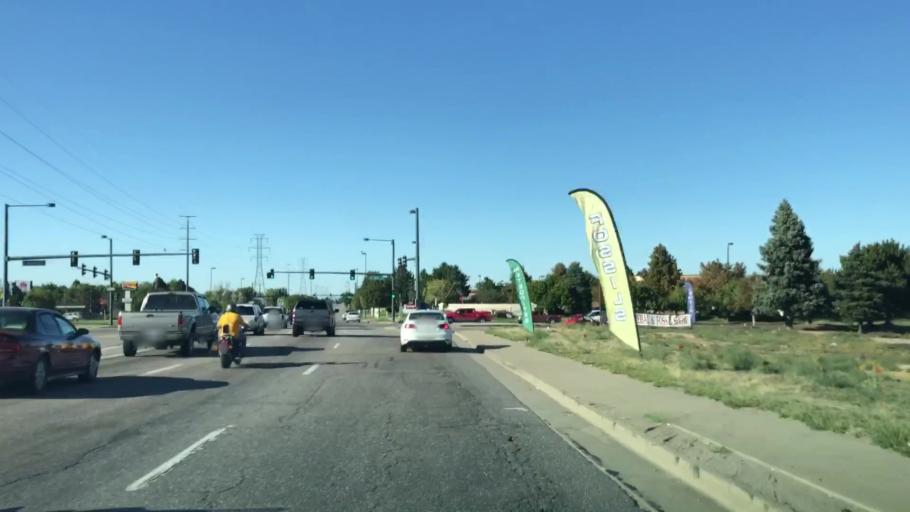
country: US
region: Colorado
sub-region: Adams County
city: Aurora
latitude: 39.7723
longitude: -104.8097
